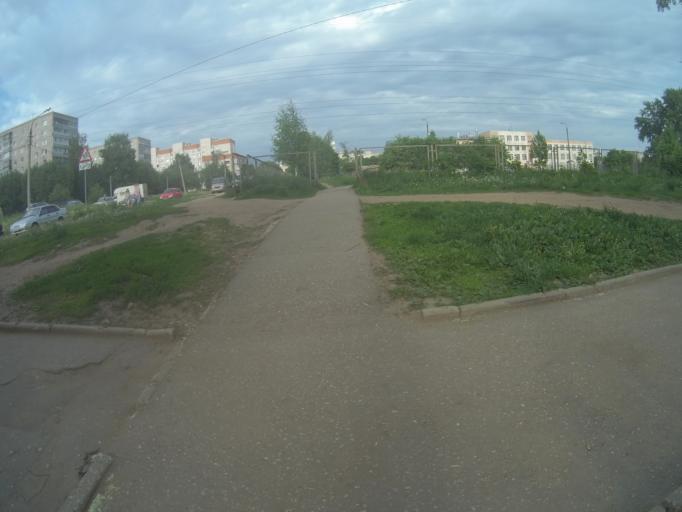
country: RU
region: Vladimir
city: Kommunar
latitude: 56.1626
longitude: 40.4507
